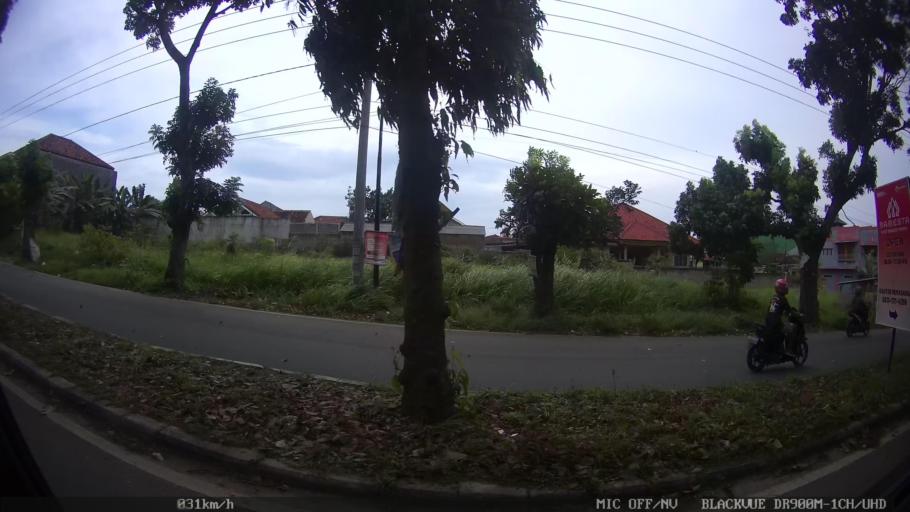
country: ID
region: Lampung
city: Kedaton
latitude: -5.3865
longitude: 105.2103
